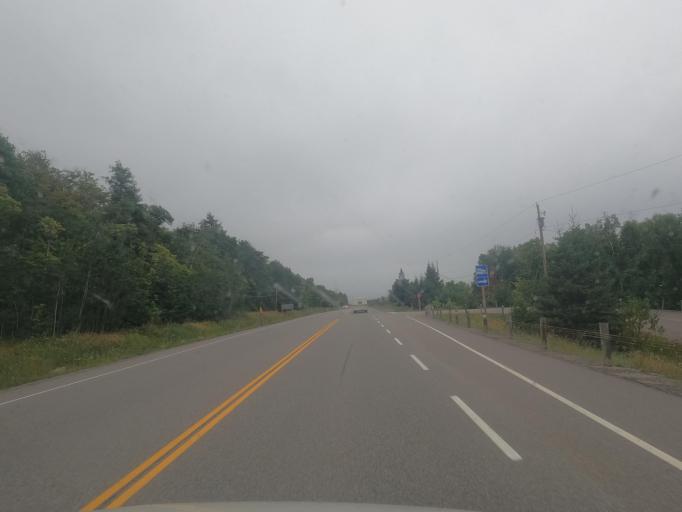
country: CA
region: Ontario
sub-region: Algoma
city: Sault Ste. Marie
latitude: 46.8422
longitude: -84.3752
